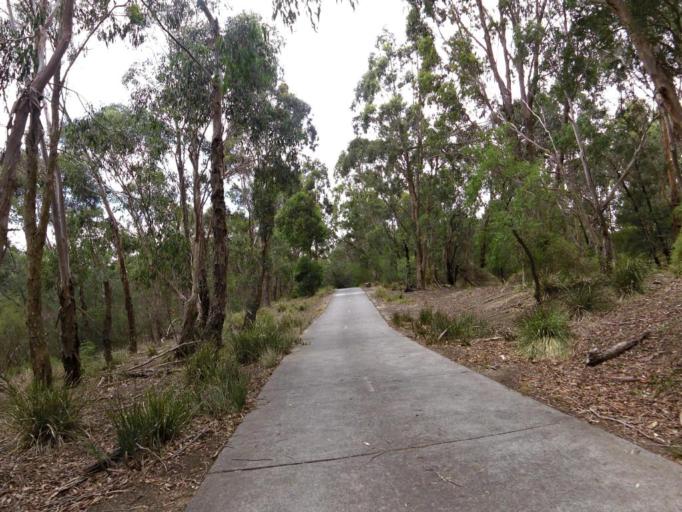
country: AU
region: Victoria
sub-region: Monash
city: Ashwood
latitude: -37.8569
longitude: 145.1031
